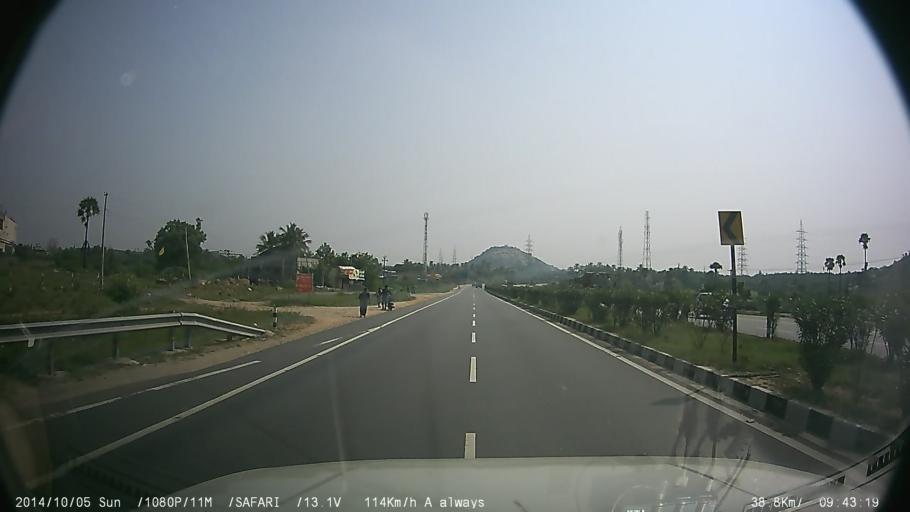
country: IN
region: Tamil Nadu
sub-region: Erode
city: Bhavani
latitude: 11.4489
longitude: 77.7584
